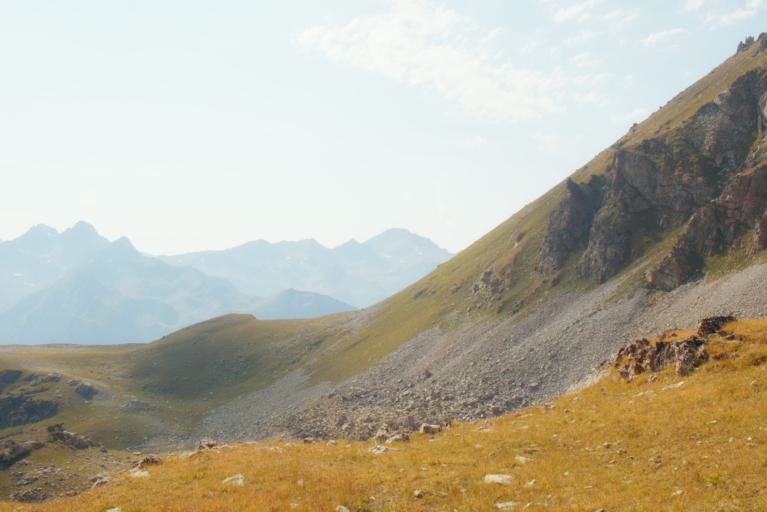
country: RU
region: Karachayevo-Cherkesiya
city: Nizhniy Arkhyz
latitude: 43.4593
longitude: 41.2062
